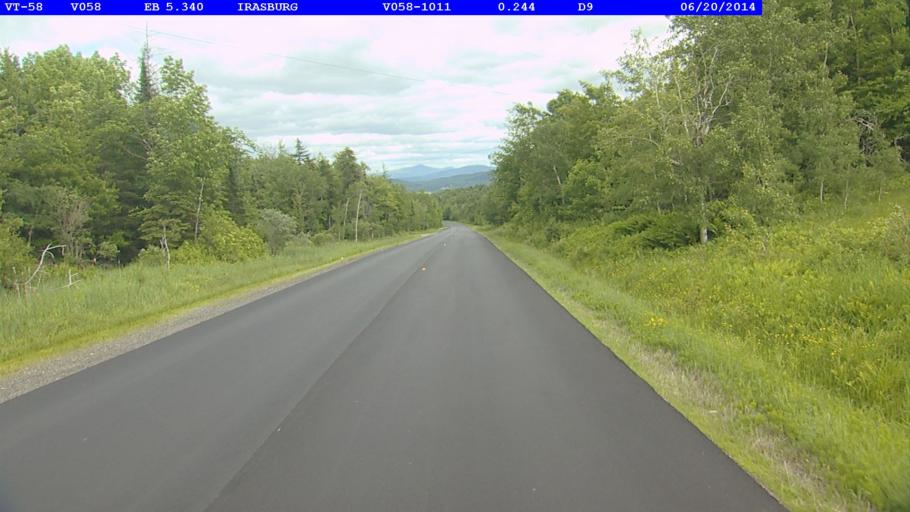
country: US
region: Vermont
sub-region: Orleans County
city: Newport
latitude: 44.8200
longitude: -72.3544
